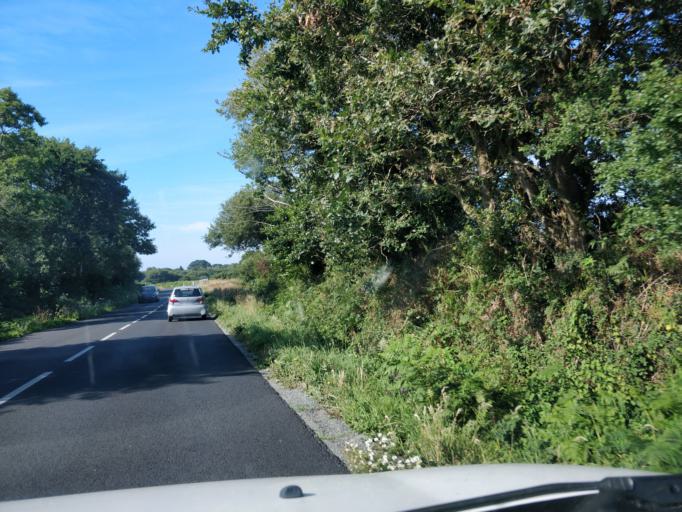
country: FR
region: Brittany
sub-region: Departement des Cotes-d'Armor
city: Tregastel
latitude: 48.7946
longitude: -3.4962
